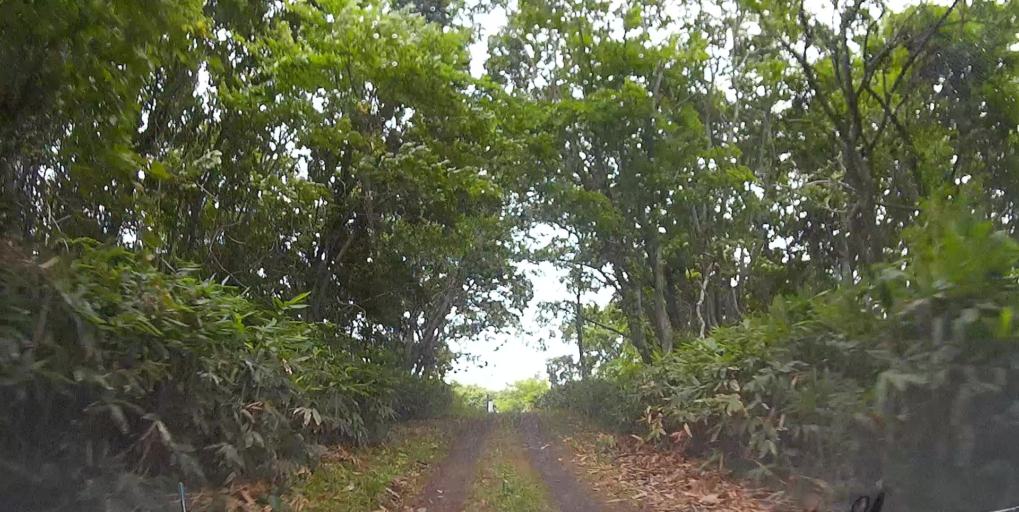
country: JP
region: Hokkaido
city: Iwanai
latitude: 42.4329
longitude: 139.9713
